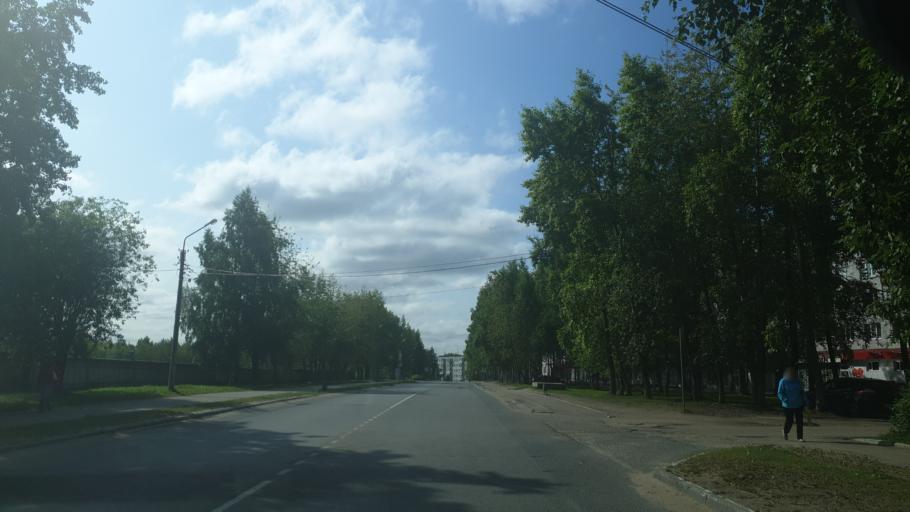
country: RU
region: Komi Republic
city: Ezhva
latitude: 61.7936
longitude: 50.7506
